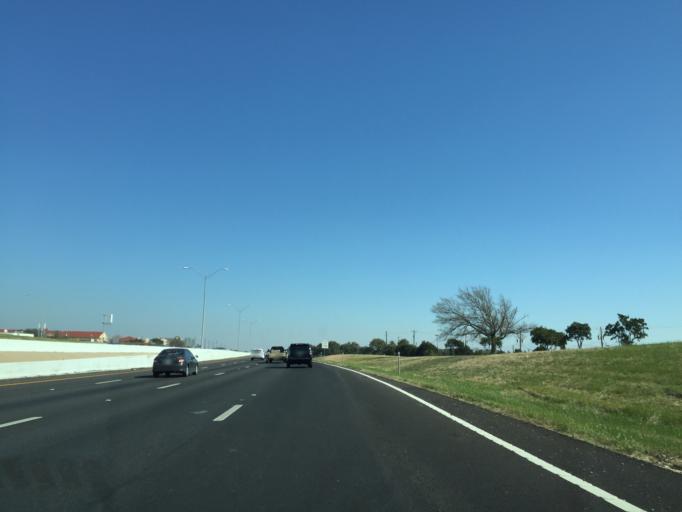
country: US
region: Texas
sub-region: Williamson County
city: Georgetown
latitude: 30.6498
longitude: -97.6793
